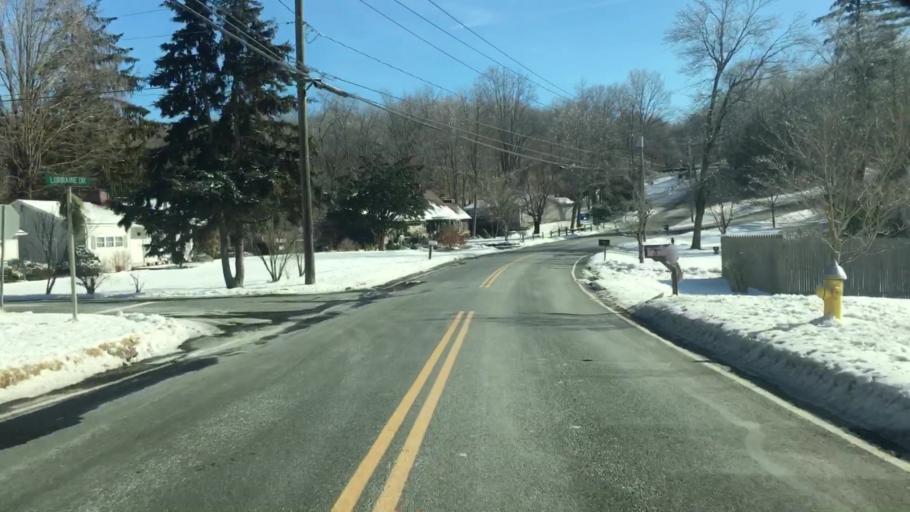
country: US
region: Connecticut
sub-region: Fairfield County
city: Trumbull
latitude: 41.3439
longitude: -73.2261
